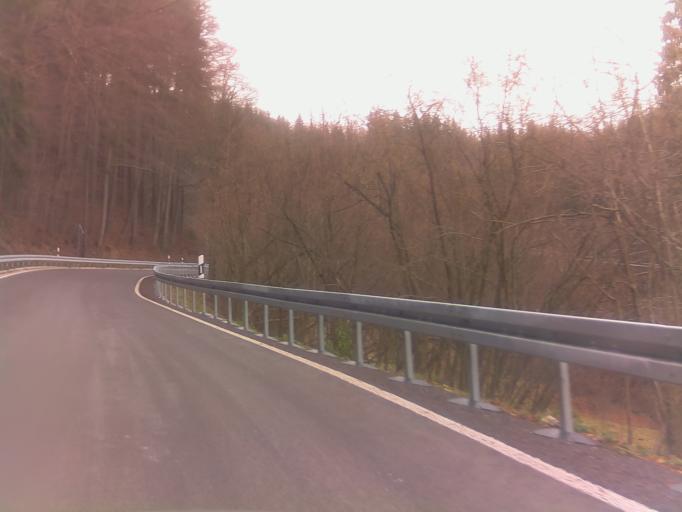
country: DE
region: Thuringia
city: Pappenheim
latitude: 50.8135
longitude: 10.4668
